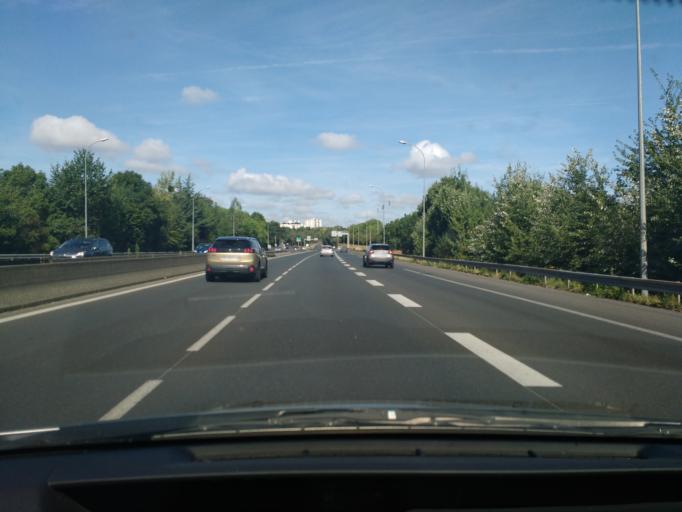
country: FR
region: Pays de la Loire
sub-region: Departement de Maine-et-Loire
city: Angers
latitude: 47.4668
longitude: -0.5825
